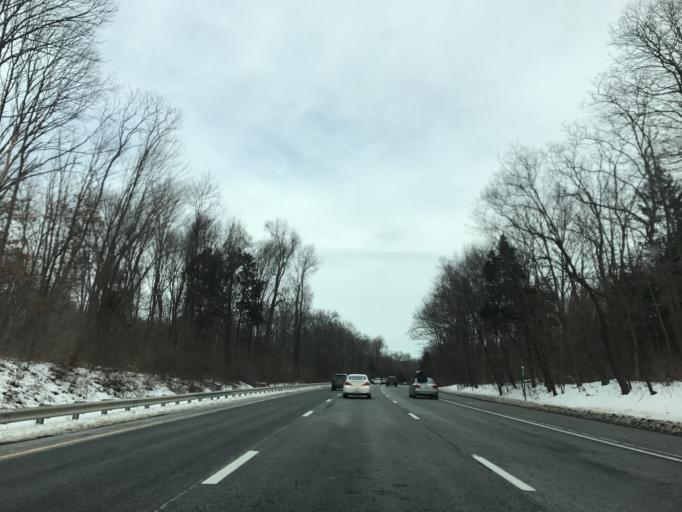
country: US
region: New Jersey
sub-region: Somerset County
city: Bernardsville
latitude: 40.7404
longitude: -74.5345
